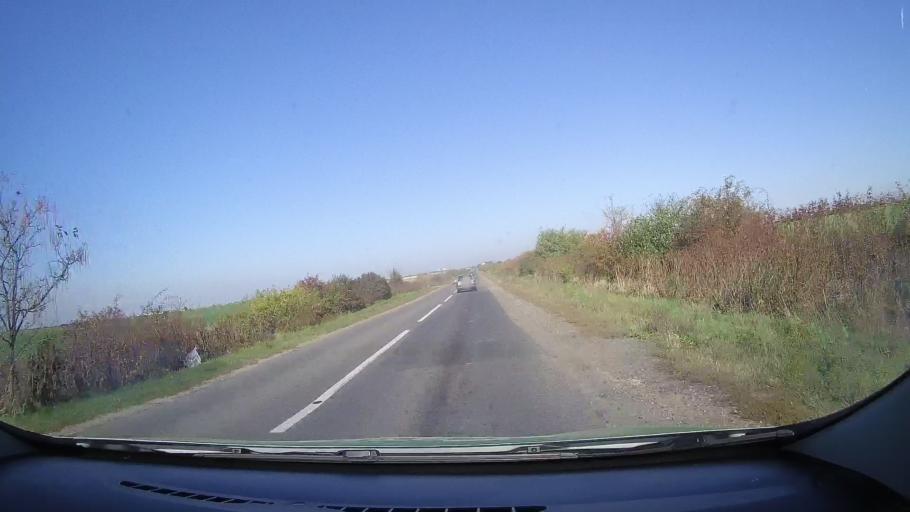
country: RO
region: Satu Mare
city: Carei
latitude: 47.6634
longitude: 22.4919
